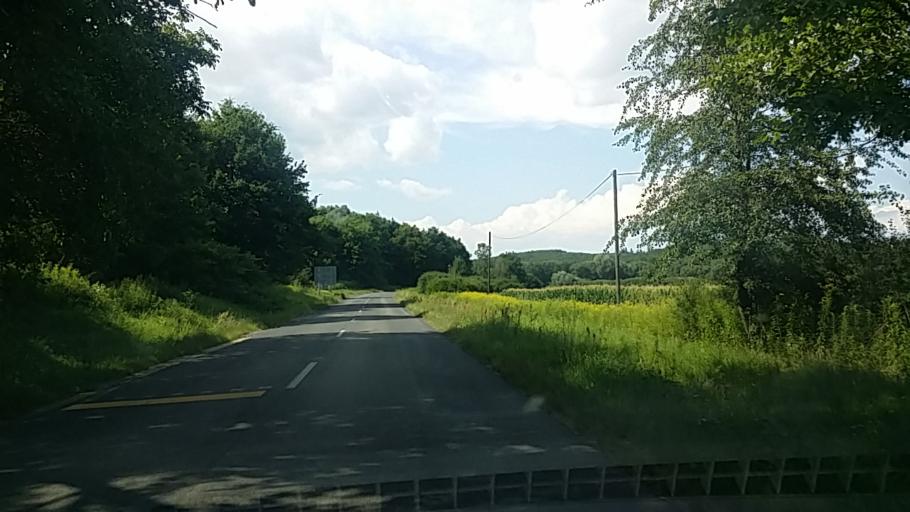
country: HU
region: Zala
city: Becsehely
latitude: 46.4542
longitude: 16.8115
